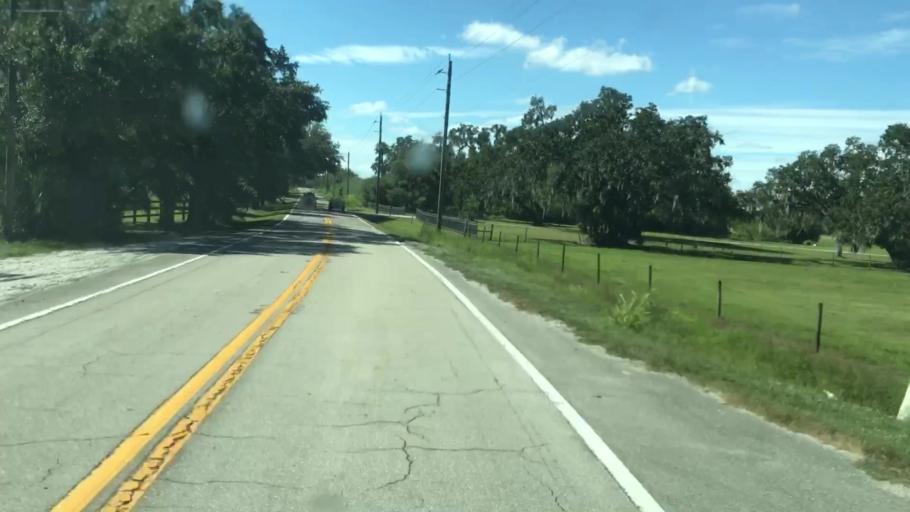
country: US
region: Florida
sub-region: Lee County
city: Olga
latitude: 26.7307
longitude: -81.7021
